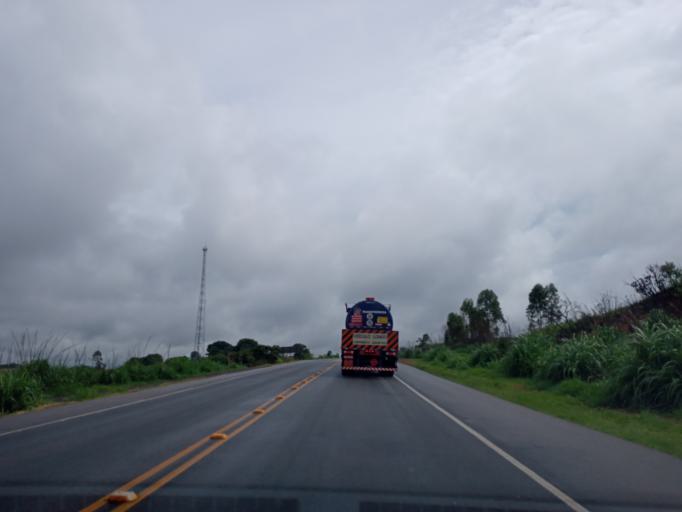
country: BR
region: Minas Gerais
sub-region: Campos Altos
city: Campos Altos
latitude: -19.7174
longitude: -46.0218
